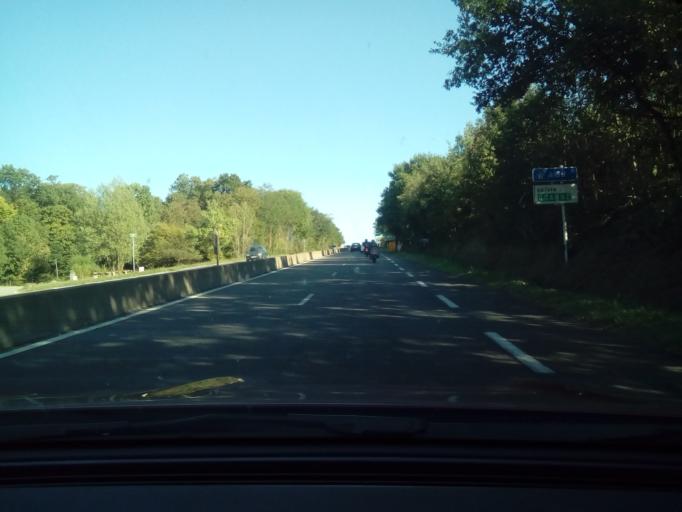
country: FR
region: Rhone-Alpes
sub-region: Departement du Rhone
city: Lissieu
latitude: 45.8388
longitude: 4.7402
